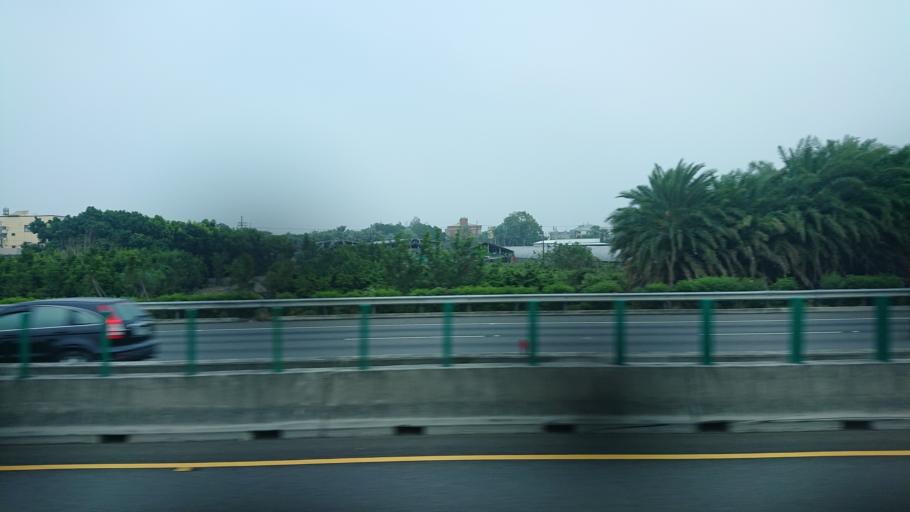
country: TW
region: Taiwan
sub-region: Changhua
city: Chang-hua
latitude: 23.9275
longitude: 120.4990
